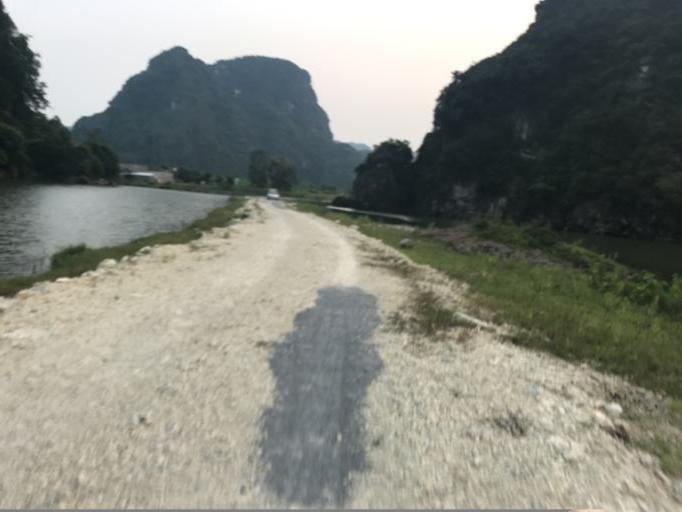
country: VN
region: Ninh Binh
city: Thi Tran Thien Ton
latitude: 20.2539
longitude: 105.9278
